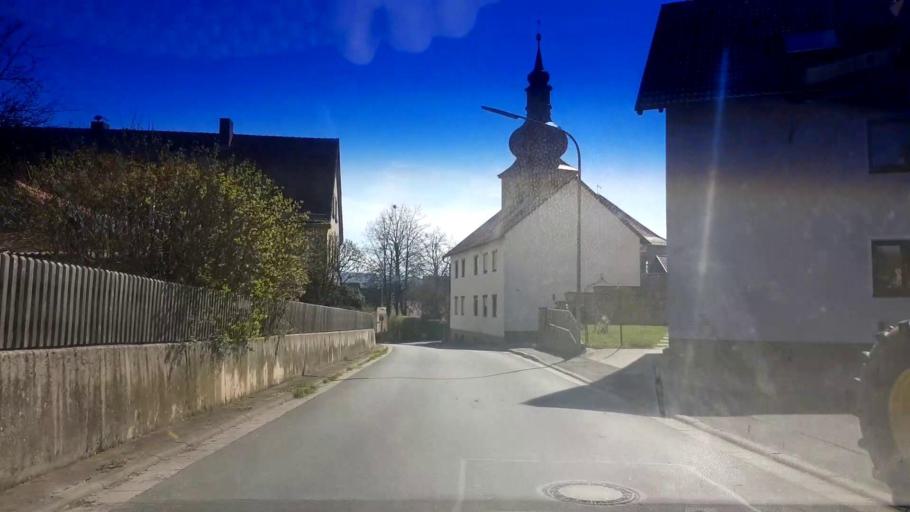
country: DE
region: Bavaria
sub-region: Upper Franconia
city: Bindlach
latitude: 50.0134
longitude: 11.6224
